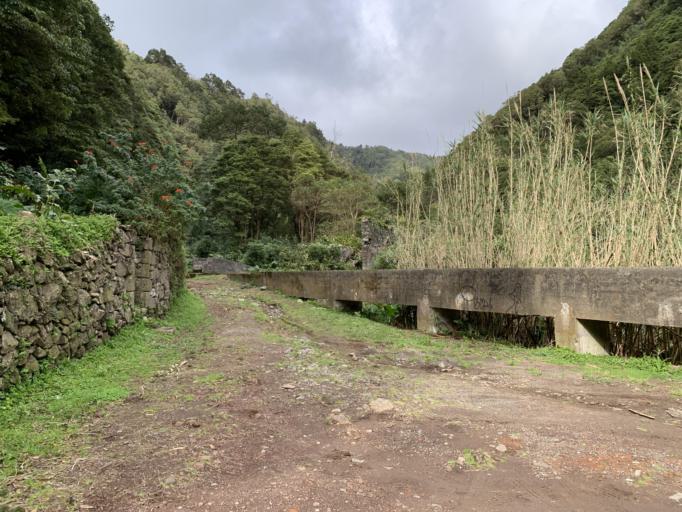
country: PT
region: Azores
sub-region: Povoacao
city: Furnas
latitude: 37.7508
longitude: -25.2022
